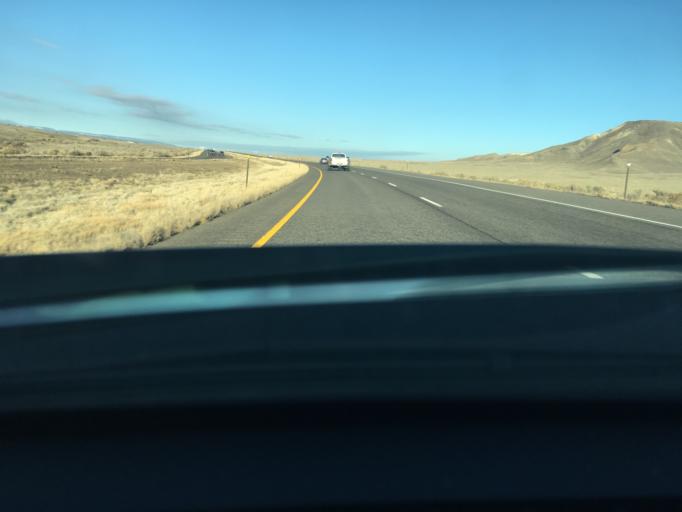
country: US
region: Colorado
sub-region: Delta County
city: Delta
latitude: 38.7765
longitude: -108.2314
